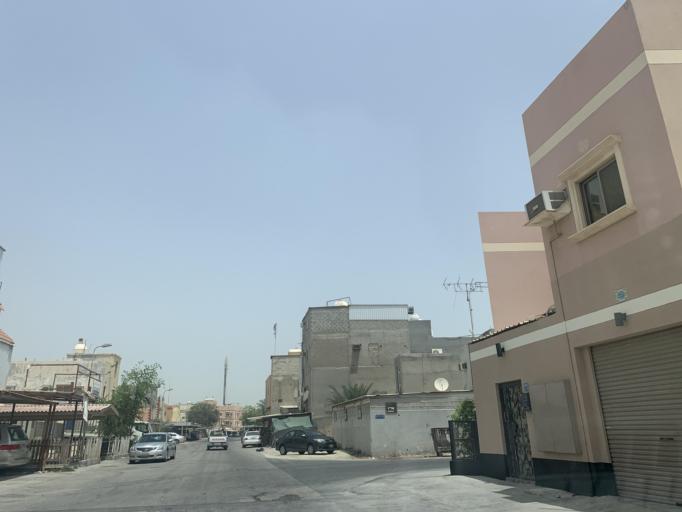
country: BH
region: Northern
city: Madinat `Isa
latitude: 26.1548
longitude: 50.5226
